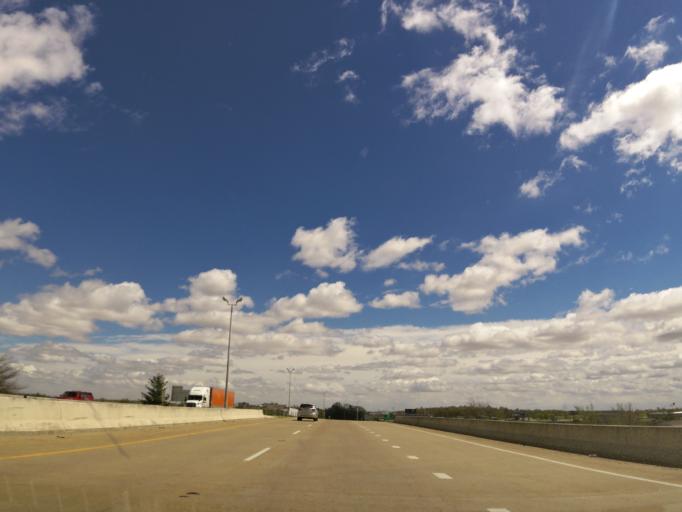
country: US
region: Arkansas
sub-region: Craighead County
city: Jonesboro
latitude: 35.8068
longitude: -90.6361
